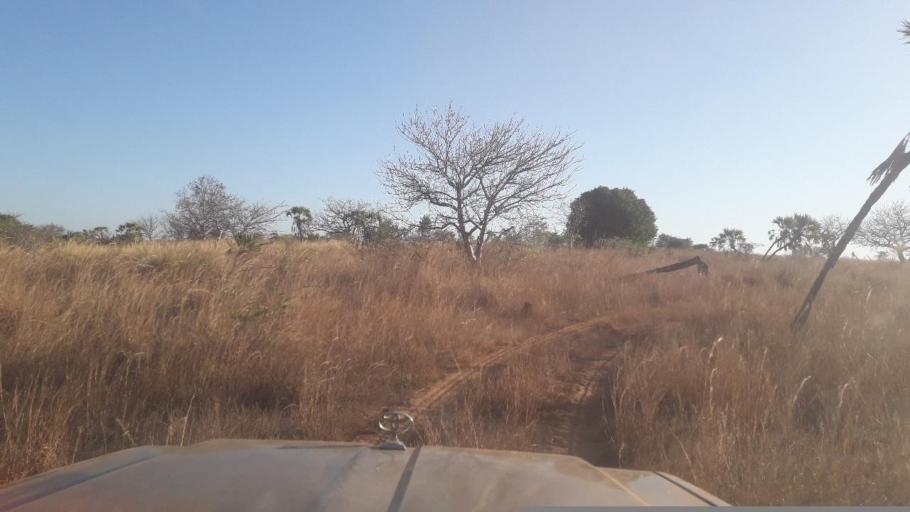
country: MG
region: Boeny
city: Sitampiky
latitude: -16.4979
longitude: 45.6065
